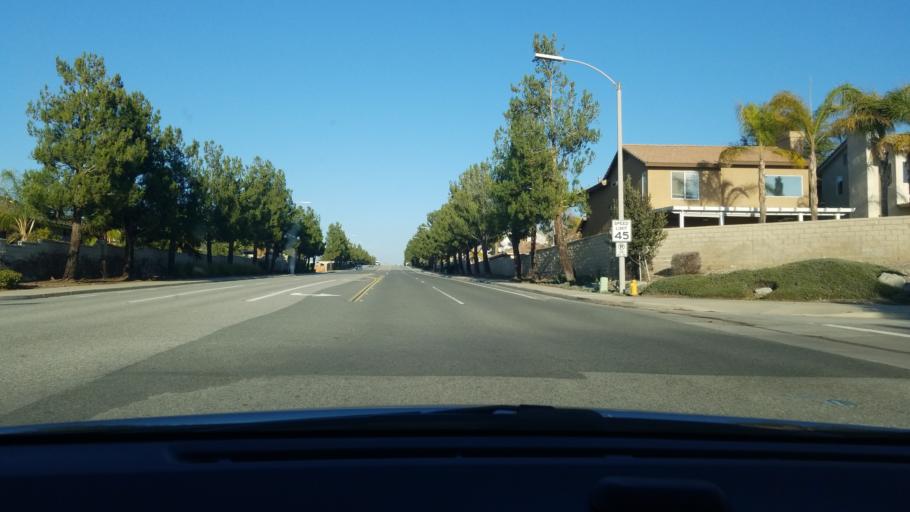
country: US
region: California
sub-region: Riverside County
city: Murrieta Hot Springs
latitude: 33.5475
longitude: -117.1518
